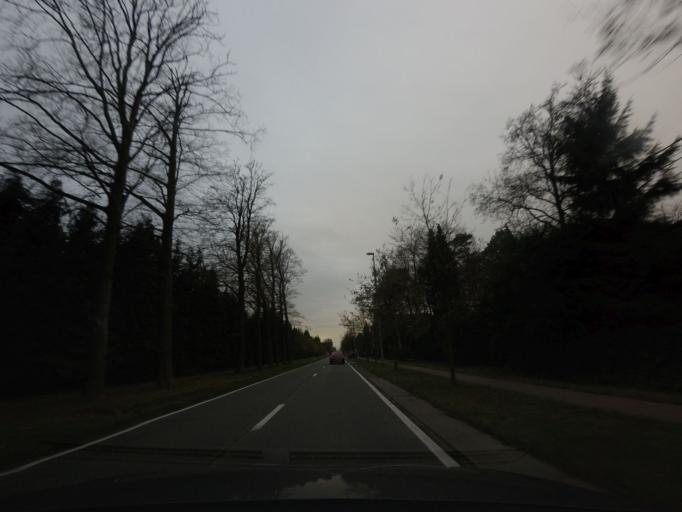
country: BE
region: Flanders
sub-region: Provincie Antwerpen
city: Brecht
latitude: 51.3260
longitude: 4.5998
